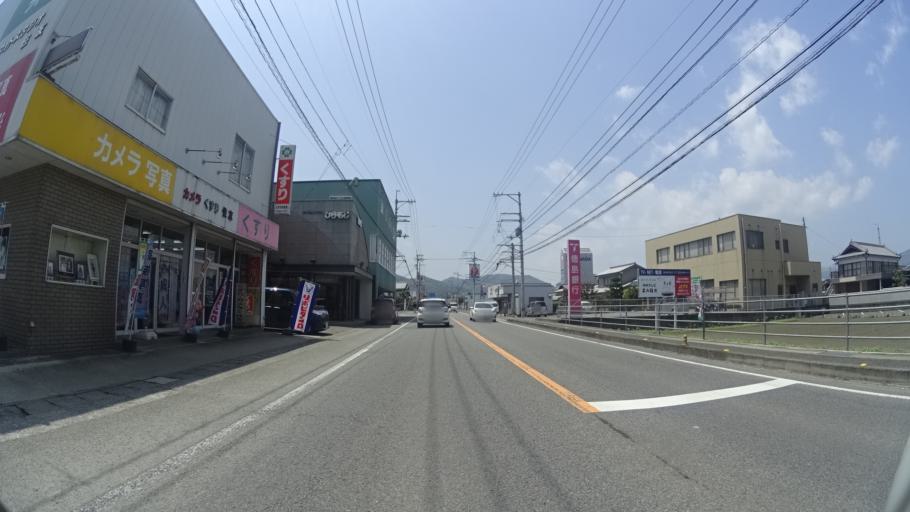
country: JP
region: Tokushima
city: Wakimachi
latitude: 34.0582
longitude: 134.2436
